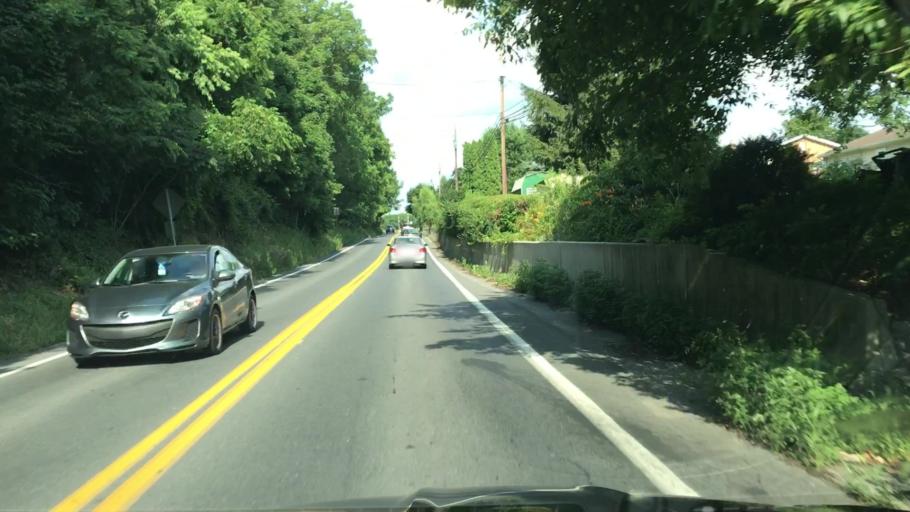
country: US
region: Pennsylvania
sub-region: Cumberland County
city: Mechanicsburg
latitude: 40.1623
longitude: -77.0101
